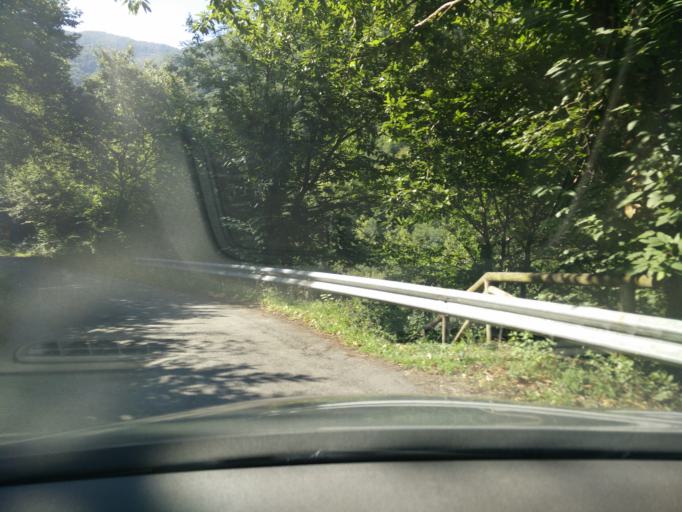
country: ES
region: Asturias
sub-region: Province of Asturias
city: Amieva
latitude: 43.1859
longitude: -5.1624
